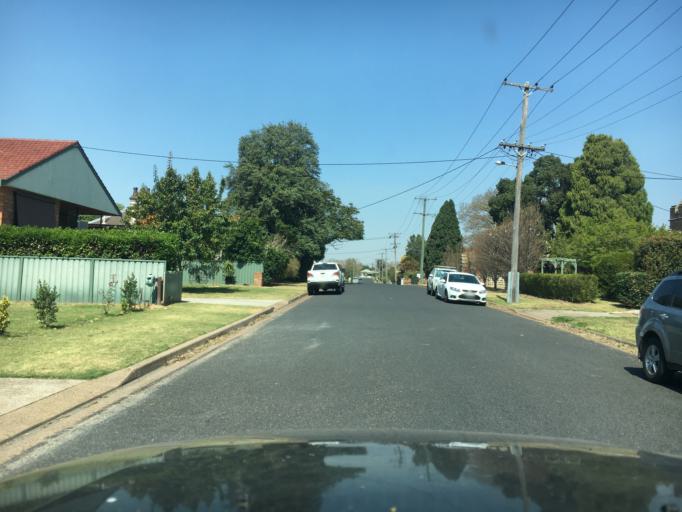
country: AU
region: New South Wales
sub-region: Singleton
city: Singleton
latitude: -32.5625
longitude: 151.1782
